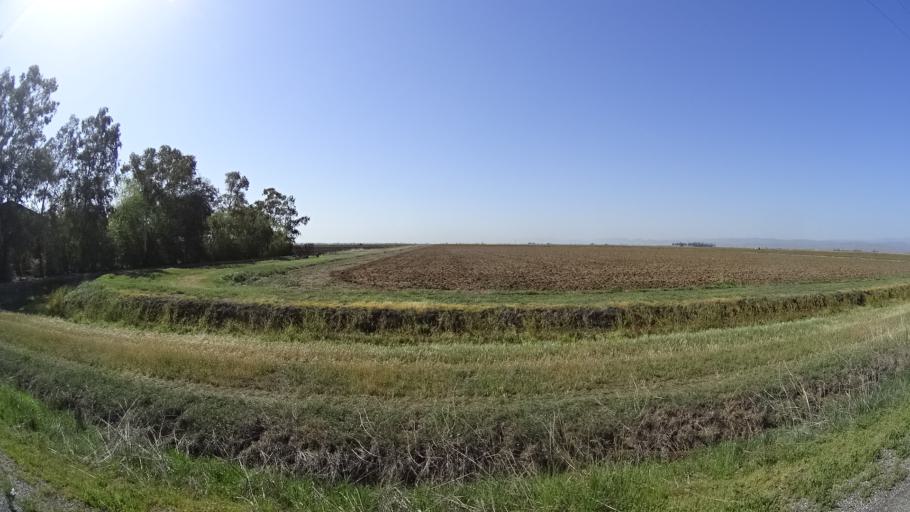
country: US
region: California
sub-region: Glenn County
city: Willows
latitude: 39.4510
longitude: -122.2026
